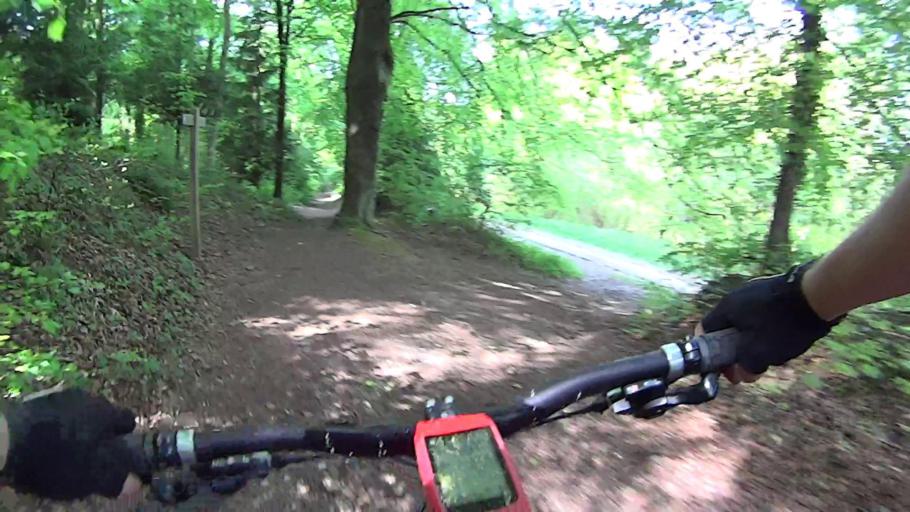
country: GB
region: England
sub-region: Hampshire
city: Petersfield
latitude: 50.9662
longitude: -0.9634
